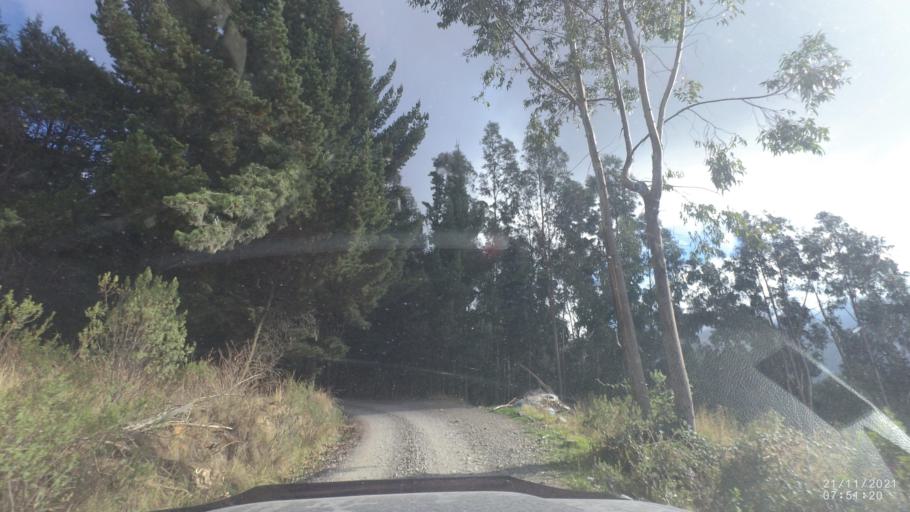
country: BO
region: Cochabamba
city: Cochabamba
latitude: -17.3060
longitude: -66.2164
